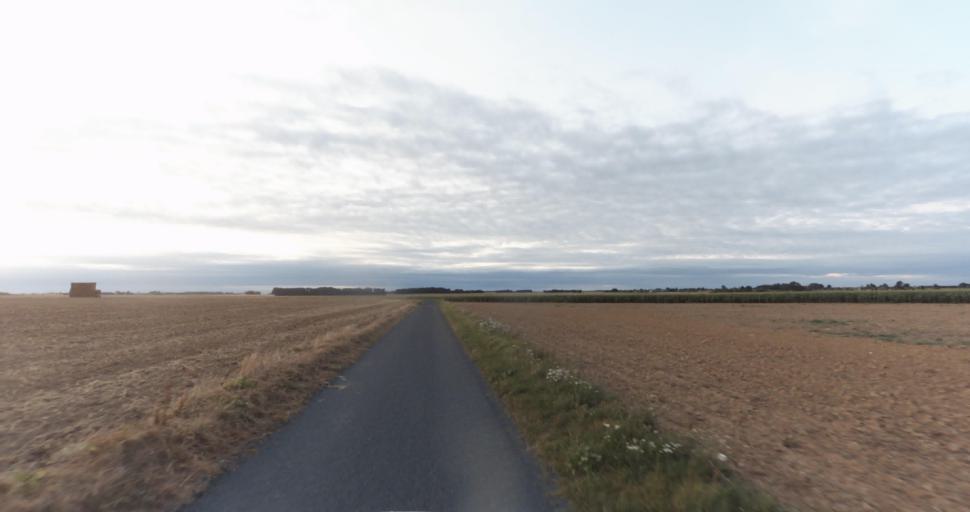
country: FR
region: Haute-Normandie
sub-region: Departement de l'Eure
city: La Madeleine-de-Nonancourt
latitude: 48.8793
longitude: 1.2284
